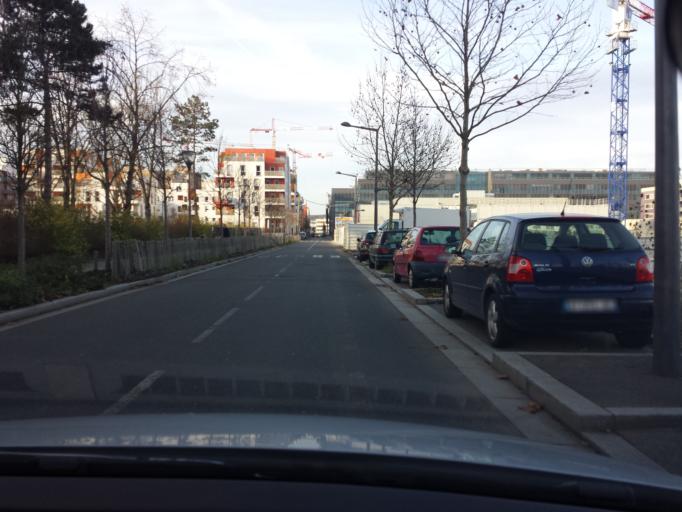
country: FR
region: Ile-de-France
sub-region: Departement de l'Essonne
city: Massy
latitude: 48.7206
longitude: 2.2677
